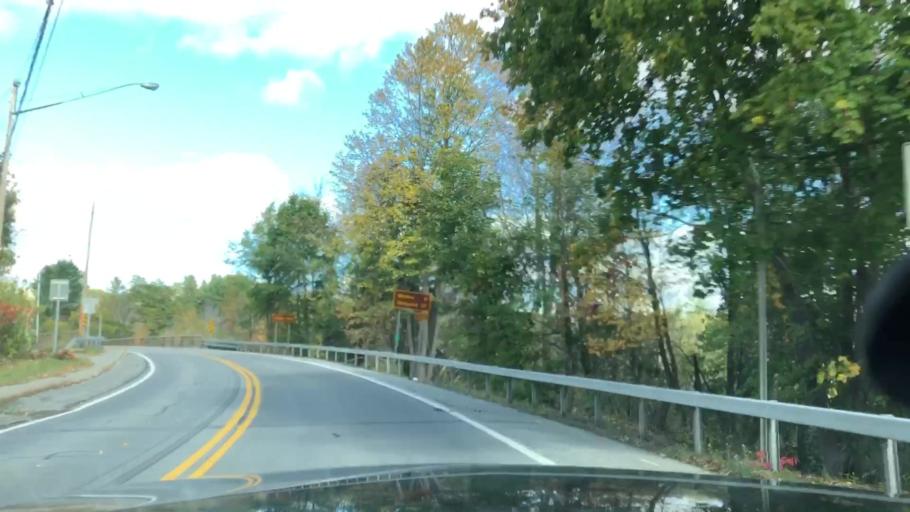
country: US
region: New York
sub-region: Warren County
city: Warrensburg
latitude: 43.6990
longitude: -73.9835
